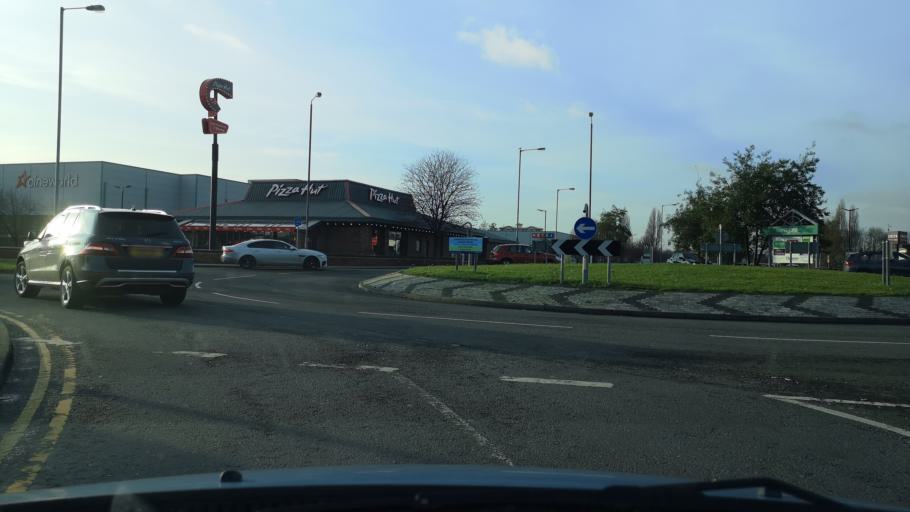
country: GB
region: England
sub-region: City and Borough of Wakefield
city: Wakefield
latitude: 53.6776
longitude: -1.5038
